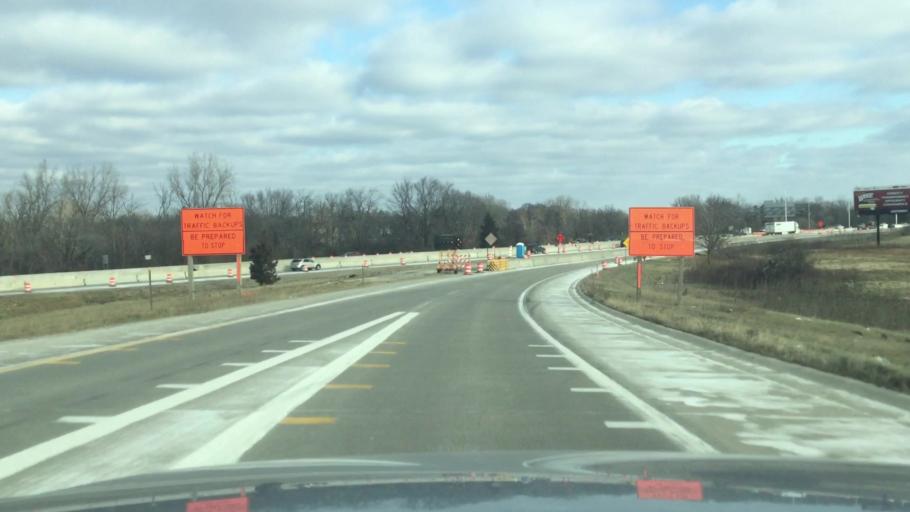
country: US
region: Michigan
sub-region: Genesee County
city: Flint
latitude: 42.9850
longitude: -83.7282
